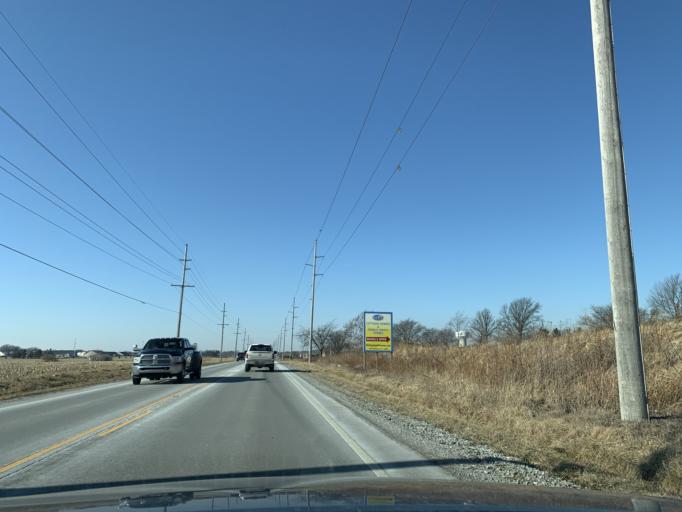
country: US
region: Indiana
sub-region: Lake County
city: Saint John
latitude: 41.4210
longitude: -87.4339
